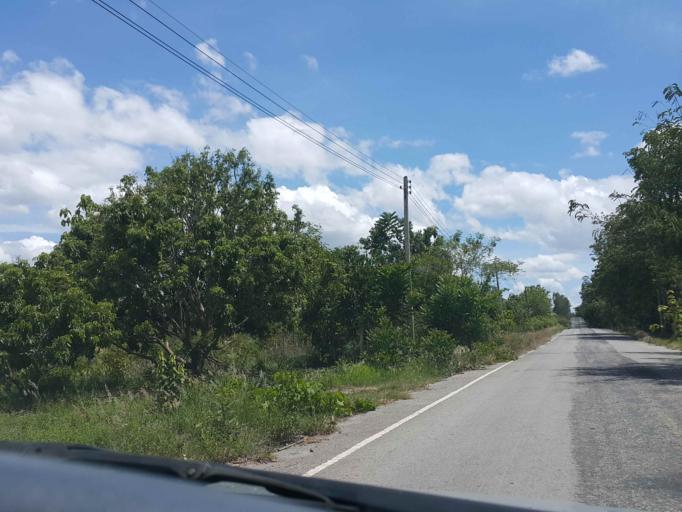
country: TH
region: Chiang Mai
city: Doi Lo
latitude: 18.5055
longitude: 98.7634
